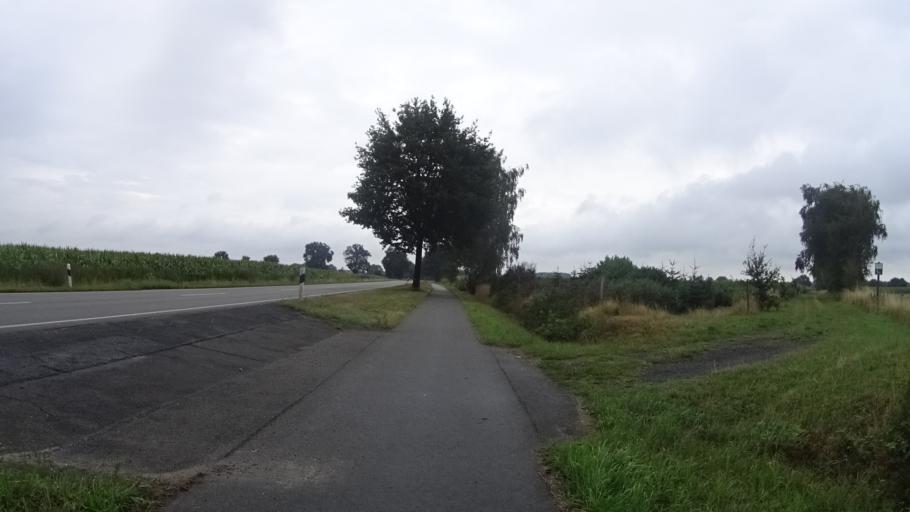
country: DE
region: Lower Saxony
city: Brinkum
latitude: 53.2731
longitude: 7.5608
